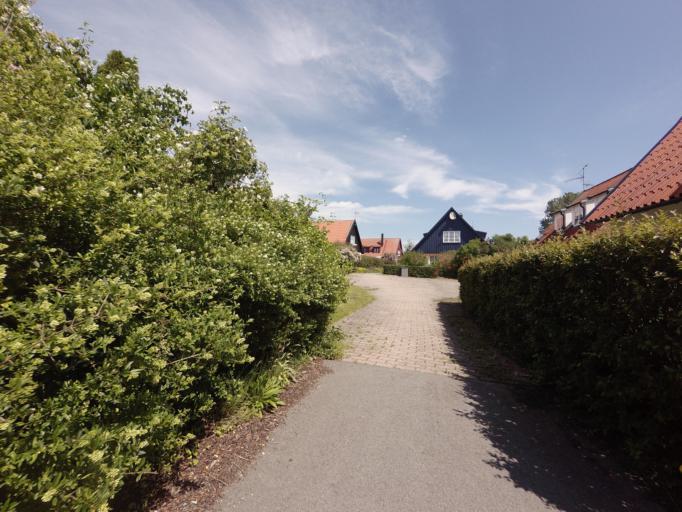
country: SE
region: Skane
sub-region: Skurups Kommun
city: Skivarp
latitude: 55.3937
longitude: 13.5970
